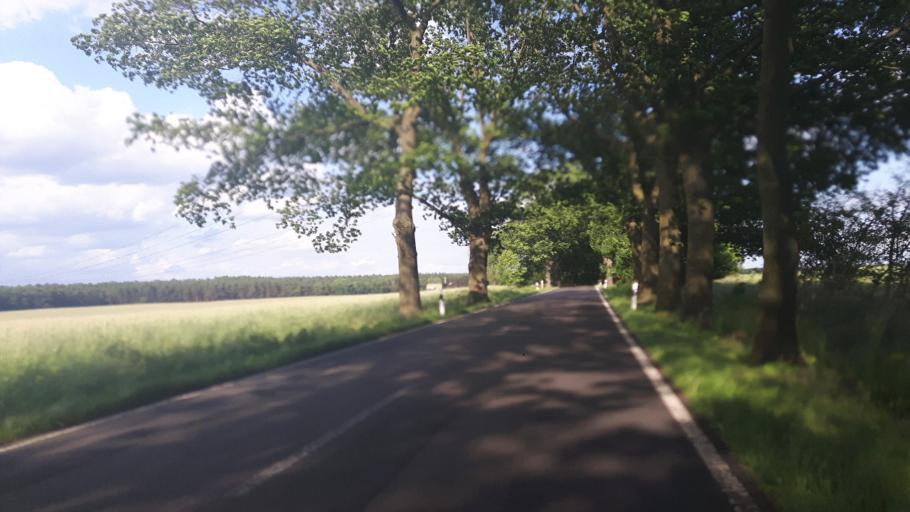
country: DE
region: Brandenburg
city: Melchow
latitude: 52.7474
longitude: 13.7412
